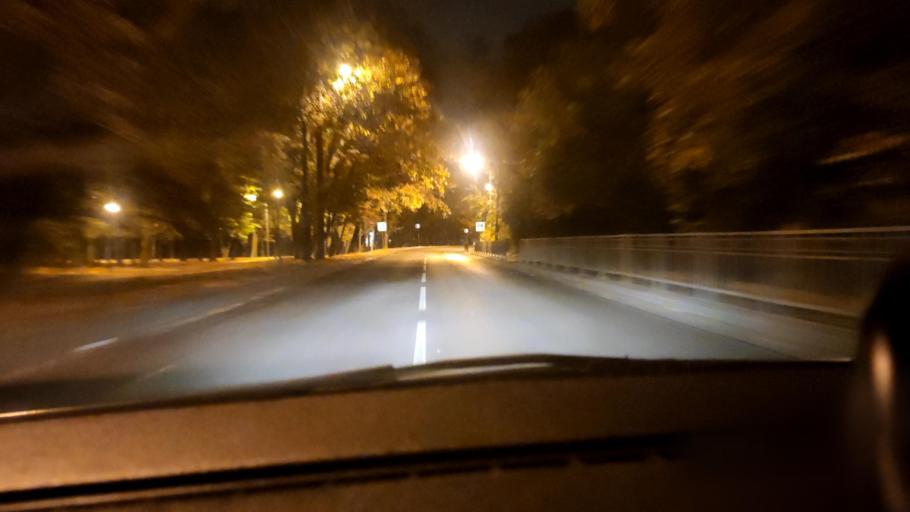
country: RU
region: Voronezj
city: Voronezh
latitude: 51.7100
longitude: 39.2265
